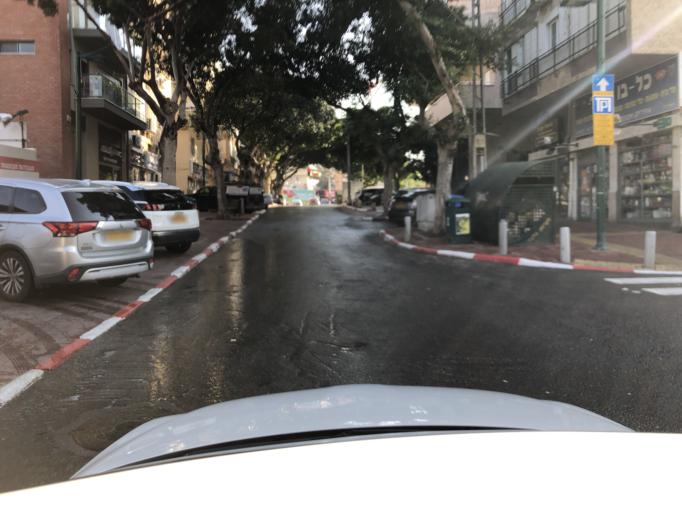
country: IL
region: Tel Aviv
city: Ramat Gan
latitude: 32.0909
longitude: 34.8187
